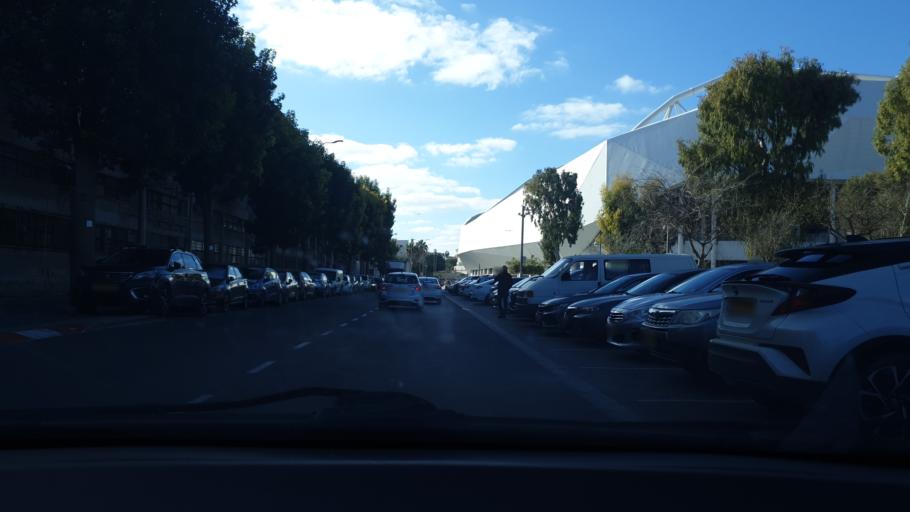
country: IL
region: Tel Aviv
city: Yafo
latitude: 32.0502
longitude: 34.7632
